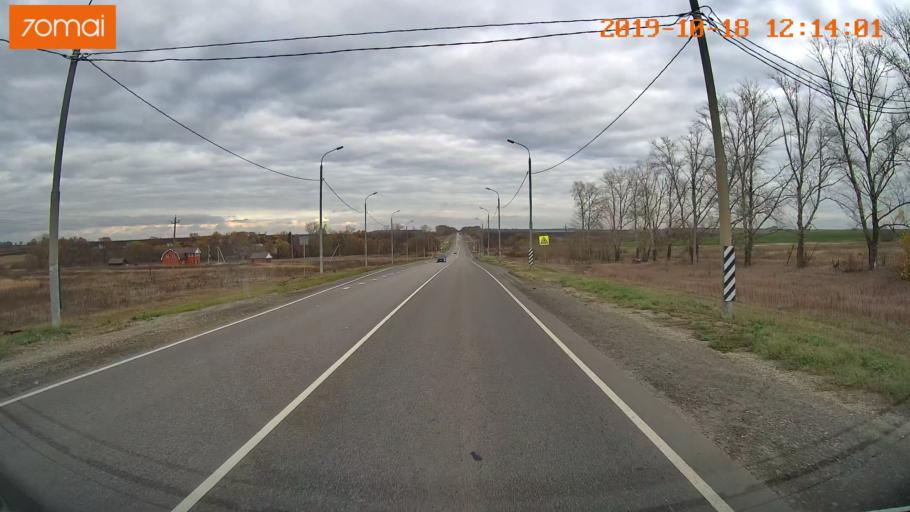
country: RU
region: Rjazan
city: Zakharovo
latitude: 54.4254
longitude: 39.3760
